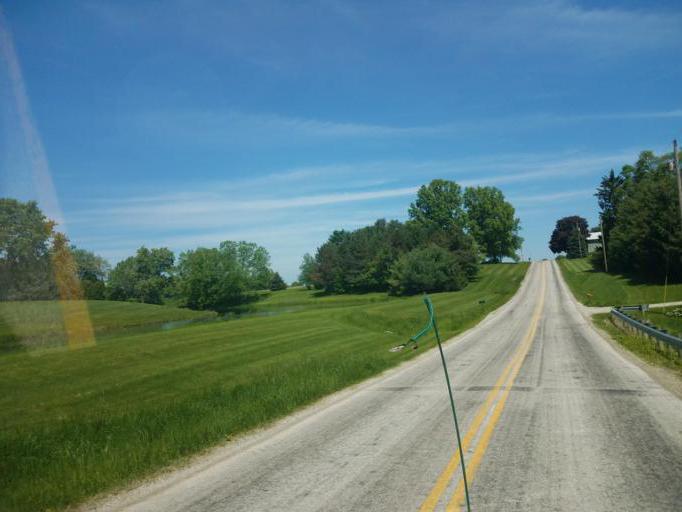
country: US
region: Ohio
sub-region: Ashland County
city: Ashland
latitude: 40.9147
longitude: -82.2432
